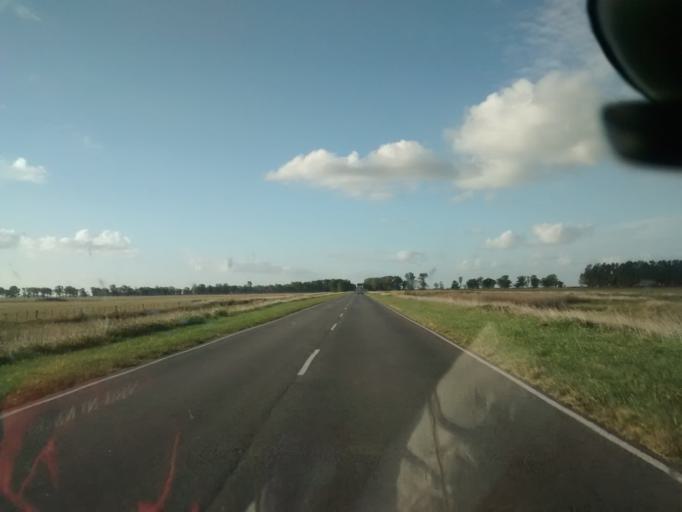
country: AR
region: Buenos Aires
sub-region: Partido de General Belgrano
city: General Belgrano
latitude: -36.1637
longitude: -58.5945
